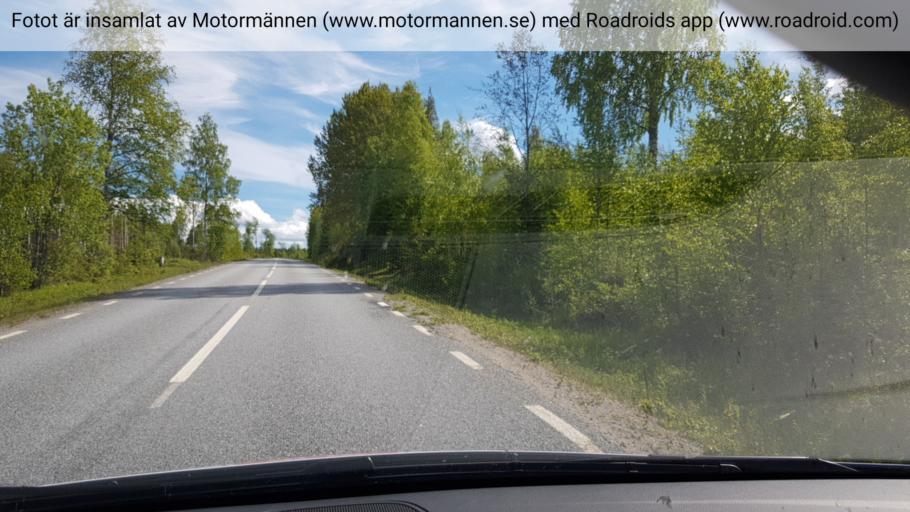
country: SE
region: Vaesterbotten
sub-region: Skelleftea Kommun
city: Burtraesk
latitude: 64.4190
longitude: 20.3910
